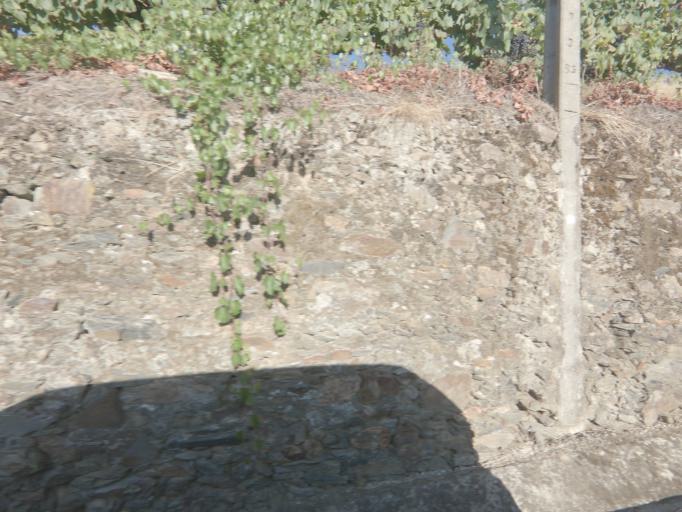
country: PT
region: Vila Real
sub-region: Peso da Regua
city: Peso da Regua
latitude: 41.1925
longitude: -7.7729
